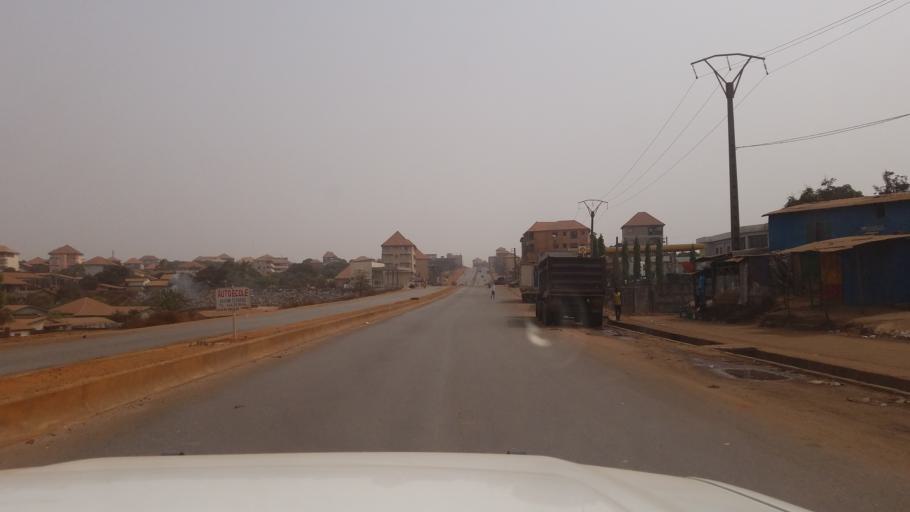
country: GN
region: Kindia
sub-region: Prefecture de Dubreka
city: Dubreka
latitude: 9.6715
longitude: -13.5553
